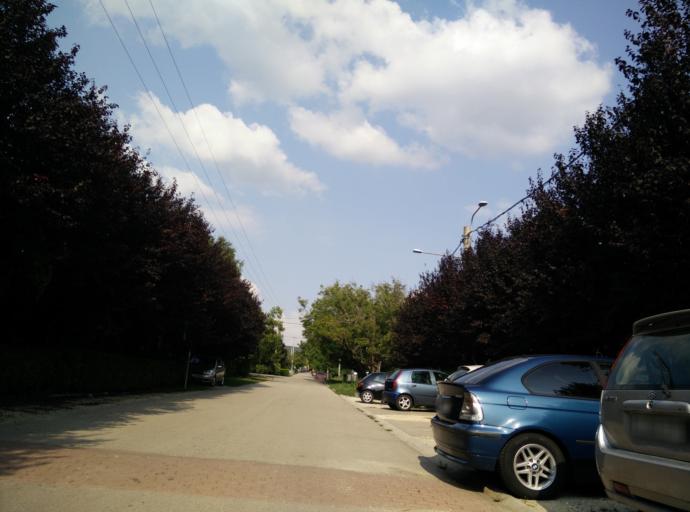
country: HU
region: Pest
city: Paty
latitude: 47.5170
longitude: 18.8256
